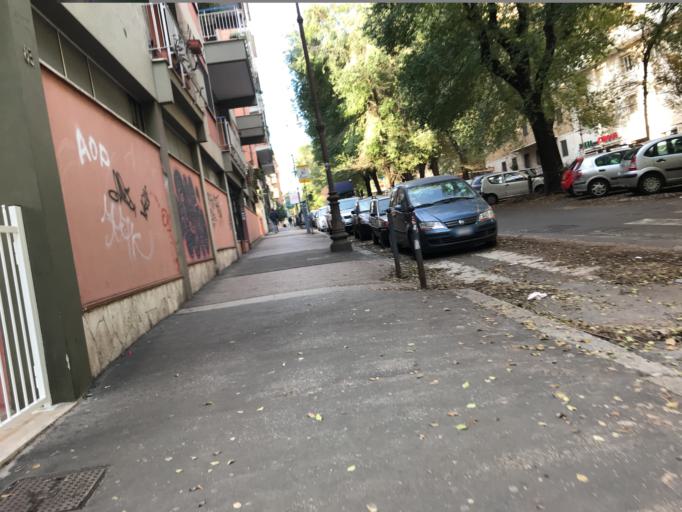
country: IT
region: Latium
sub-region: Citta metropolitana di Roma Capitale
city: Rome
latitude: 41.9078
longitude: 12.5183
